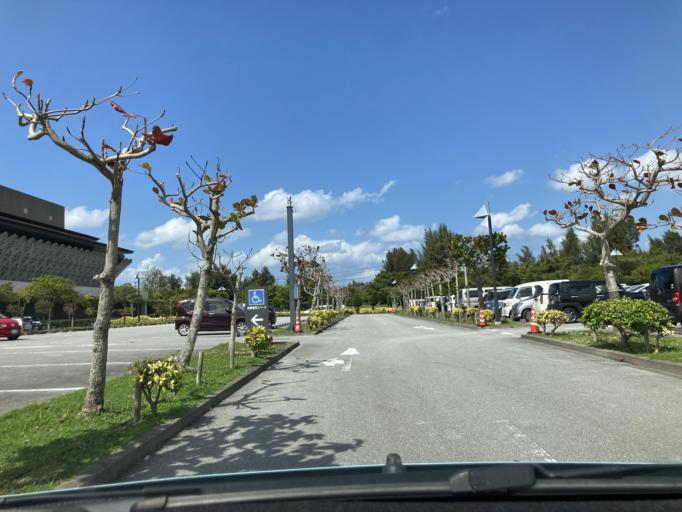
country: JP
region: Okinawa
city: Naha-shi
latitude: 26.2468
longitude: 127.6897
